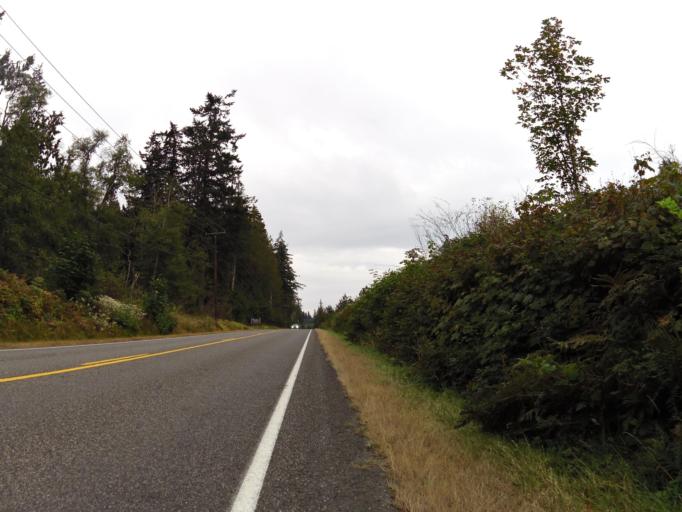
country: US
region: Washington
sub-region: Jefferson County
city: Port Ludlow
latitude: 47.9770
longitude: -122.7102
